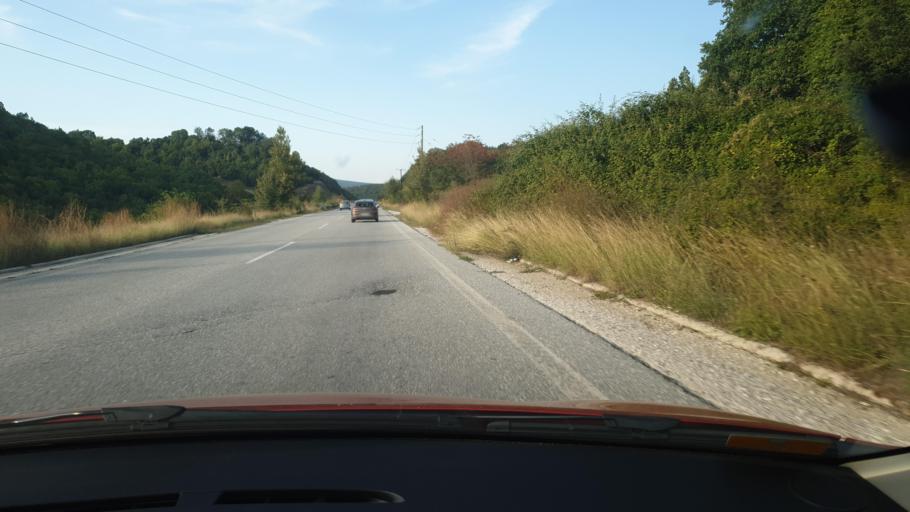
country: GR
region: Central Macedonia
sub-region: Nomos Chalkidikis
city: Polygyros
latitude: 40.4334
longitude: 23.4170
